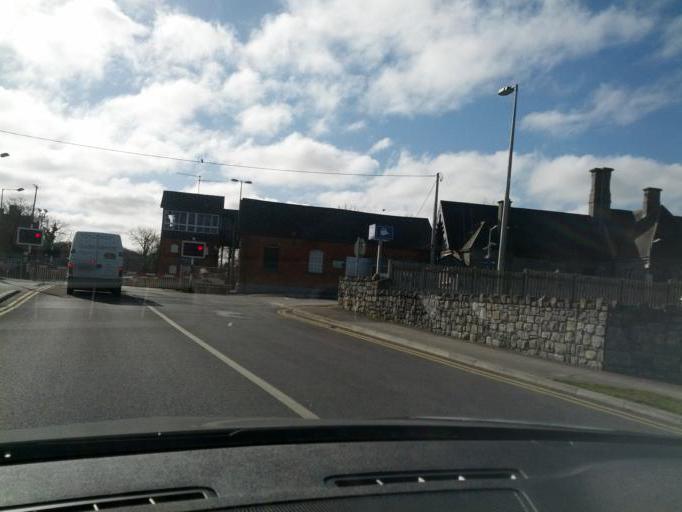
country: IE
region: Connaught
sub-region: County Galway
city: Ballinasloe
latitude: 53.3369
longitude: -8.2396
